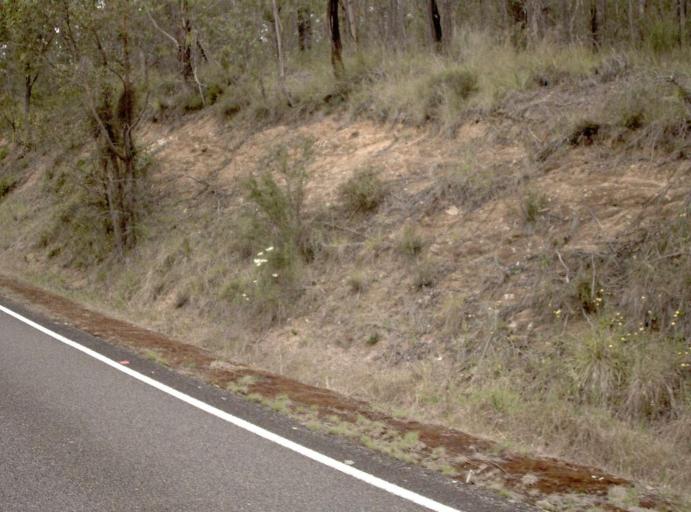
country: AU
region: New South Wales
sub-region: Bombala
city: Bombala
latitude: -37.2786
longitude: 149.2238
